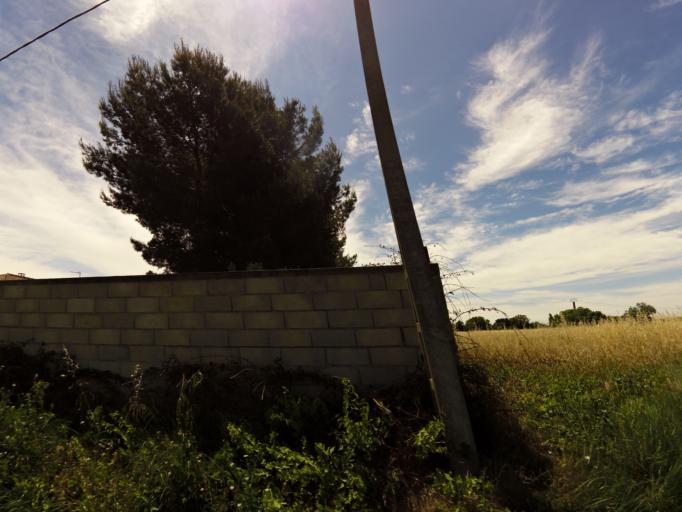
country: FR
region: Languedoc-Roussillon
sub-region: Departement du Gard
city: Bernis
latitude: 43.7651
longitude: 4.2949
